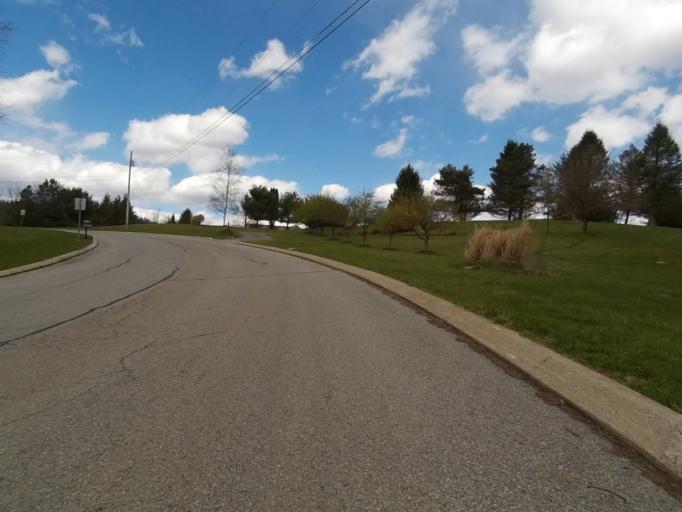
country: US
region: Pennsylvania
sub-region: Centre County
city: Park Forest Village
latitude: 40.8288
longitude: -77.9455
